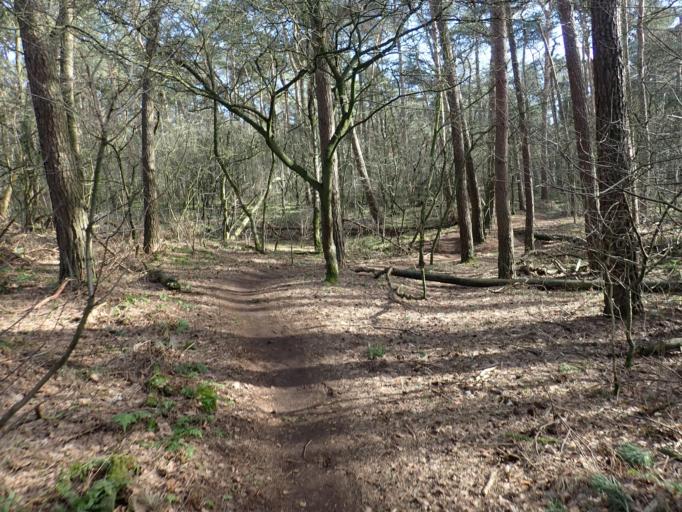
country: BE
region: Flanders
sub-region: Provincie Antwerpen
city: Brecht
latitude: 51.2985
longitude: 4.6357
